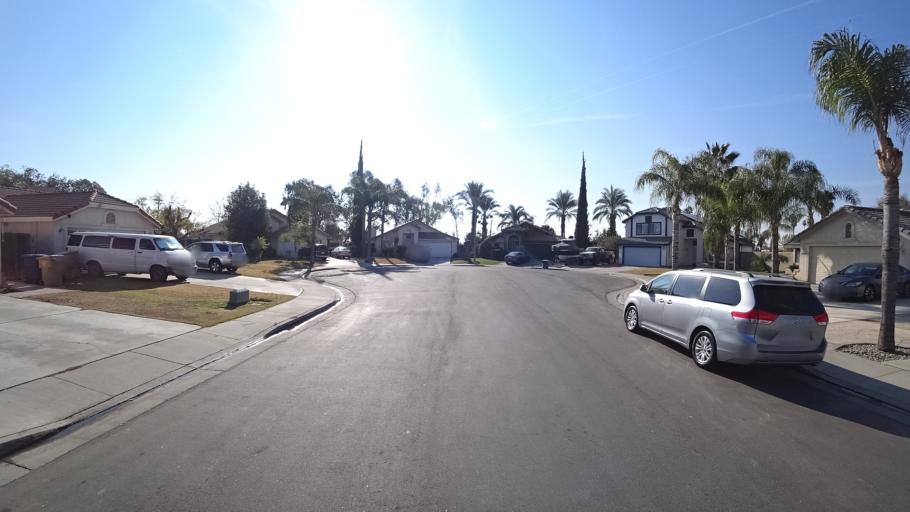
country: US
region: California
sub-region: Kern County
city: Greenfield
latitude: 35.3112
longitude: -119.0227
